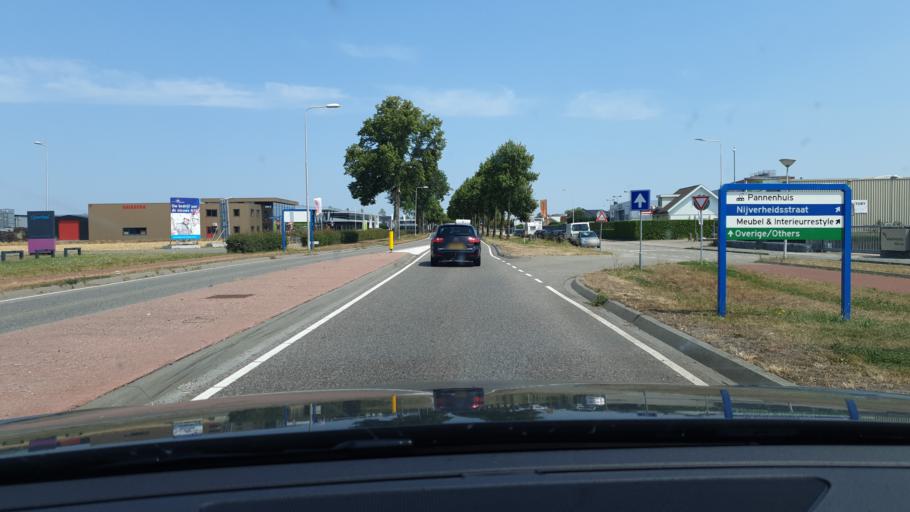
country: NL
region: Gelderland
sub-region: Gemeente Arnhem
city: Arnhem
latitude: 51.9115
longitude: 5.9161
